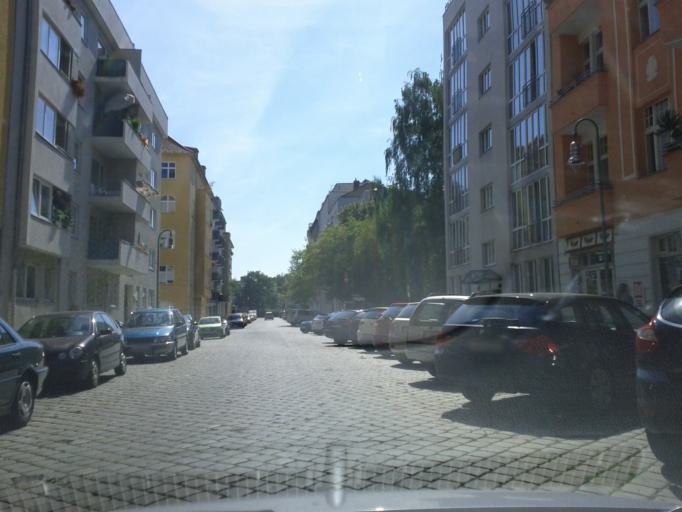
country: DE
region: Berlin
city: Moabit
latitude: 52.5202
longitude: 13.3323
